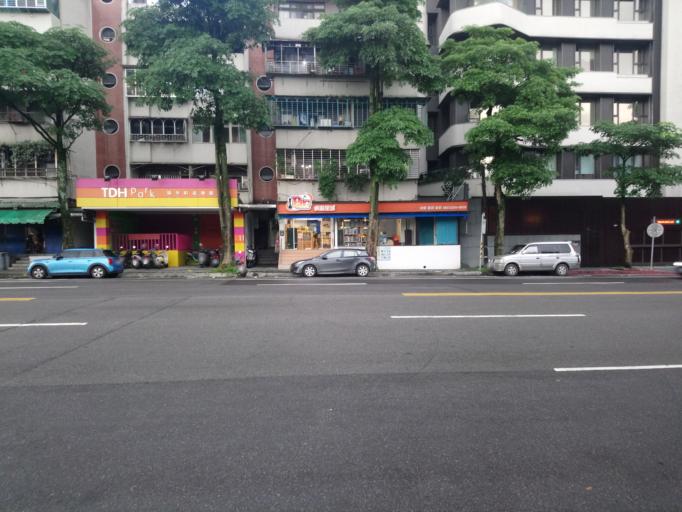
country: TW
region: Taipei
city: Taipei
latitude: 24.9932
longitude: 121.5737
